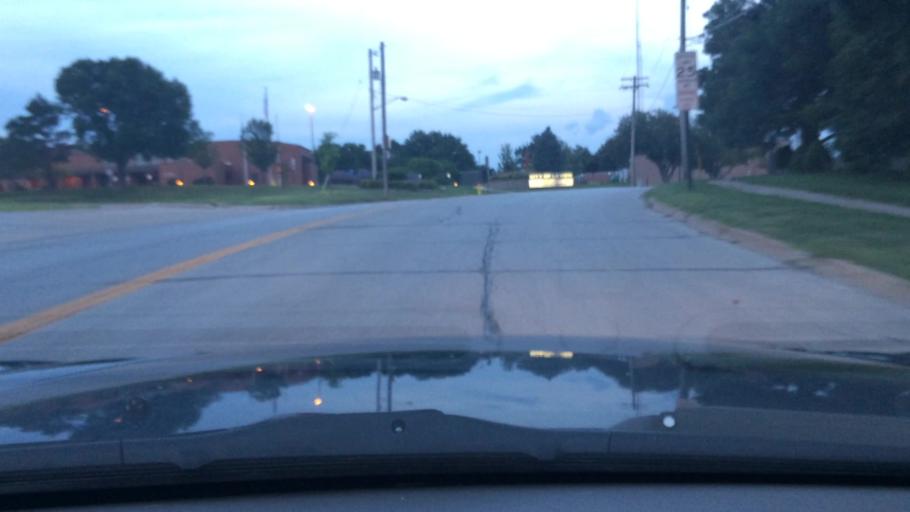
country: US
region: Nebraska
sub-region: Sarpy County
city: La Vista
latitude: 41.1876
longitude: -96.0406
